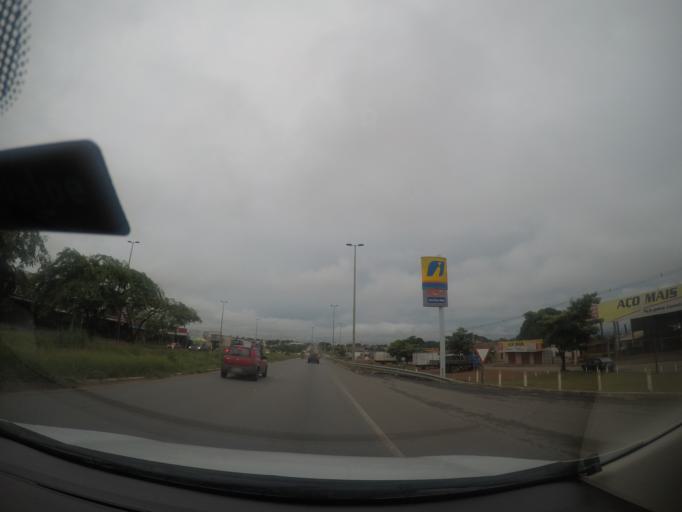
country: BR
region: Goias
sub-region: Aparecida De Goiania
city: Aparecida de Goiania
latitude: -16.7614
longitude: -49.3456
